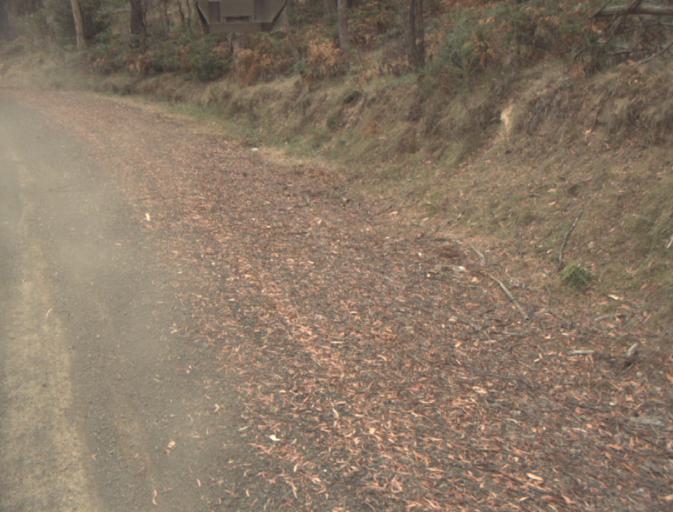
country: AU
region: Tasmania
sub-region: Northern Midlands
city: Evandale
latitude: -41.4926
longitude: 147.5476
